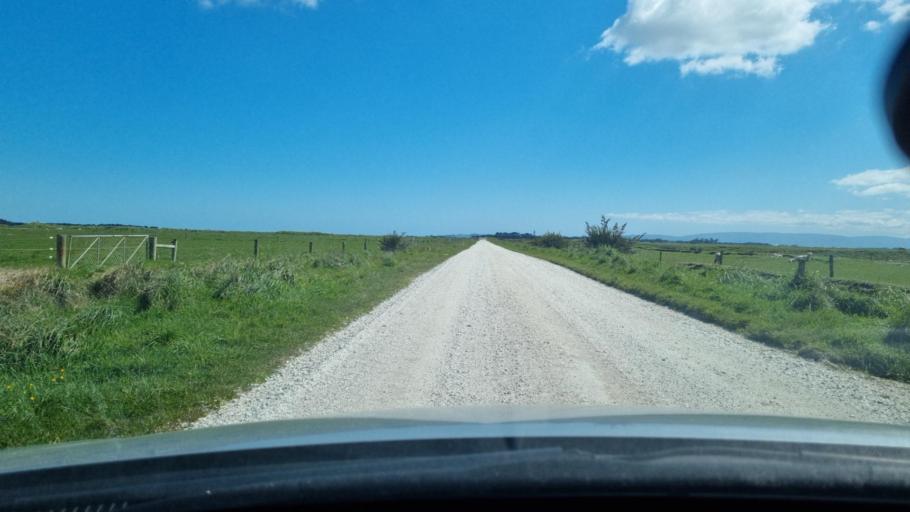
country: NZ
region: Southland
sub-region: Invercargill City
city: Invercargill
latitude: -46.3693
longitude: 168.2597
